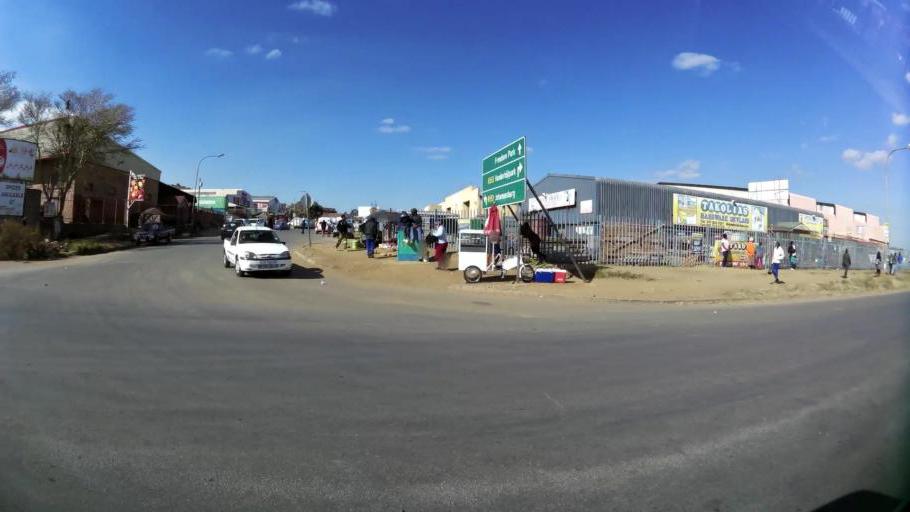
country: ZA
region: Gauteng
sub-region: City of Johannesburg Metropolitan Municipality
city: Soweto
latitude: -26.2790
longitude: 27.9330
